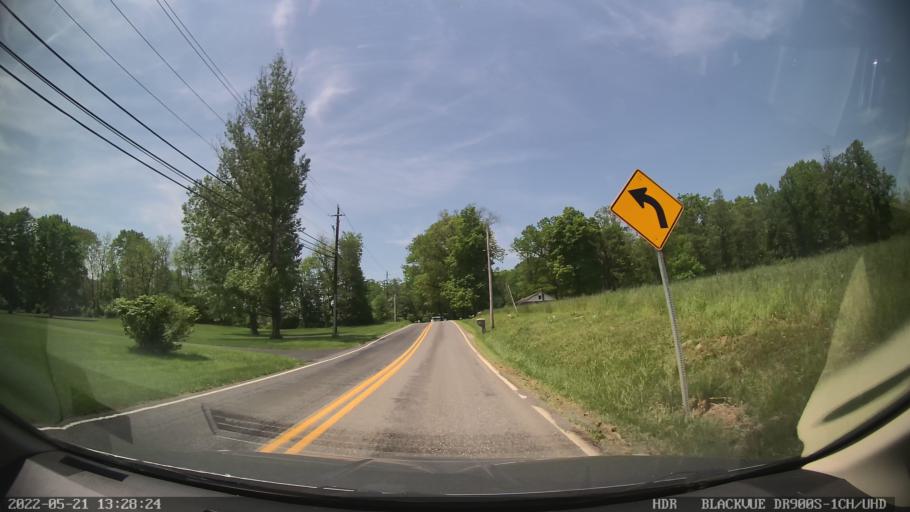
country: US
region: Pennsylvania
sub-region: Berks County
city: Bally
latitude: 40.4215
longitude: -75.6253
